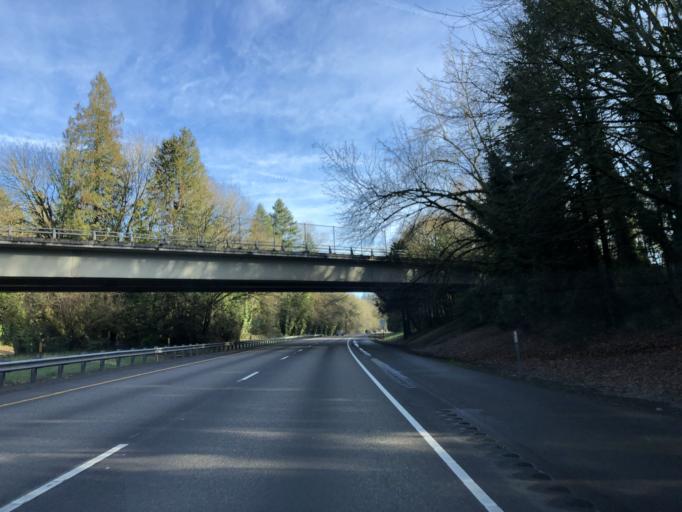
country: US
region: Oregon
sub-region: Clackamas County
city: Stafford
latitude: 45.3662
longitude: -122.6845
